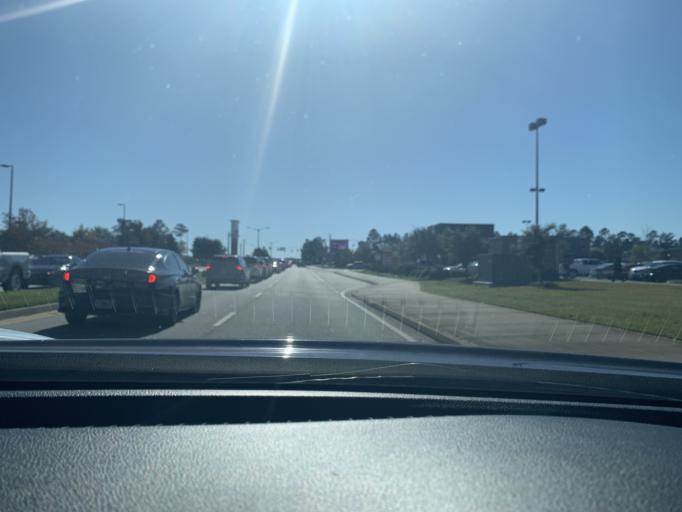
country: US
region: Georgia
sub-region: Chatham County
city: Pooler
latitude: 32.1428
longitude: -81.2474
